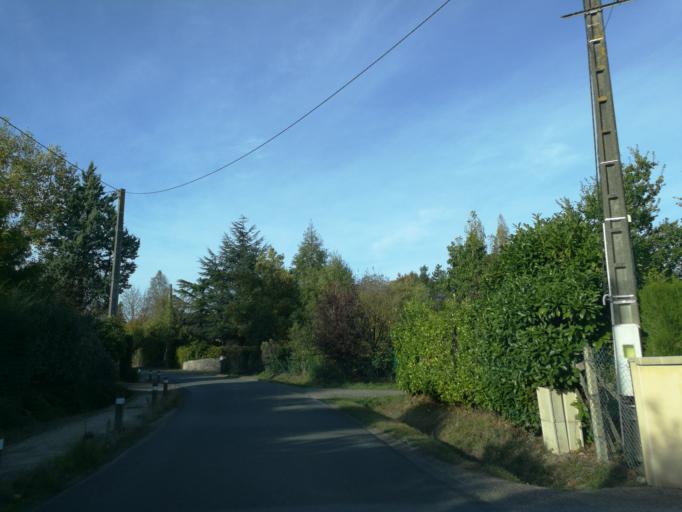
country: FR
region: Brittany
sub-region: Departement d'Ille-et-Vilaine
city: Bedee
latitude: 48.1921
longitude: -1.9485
